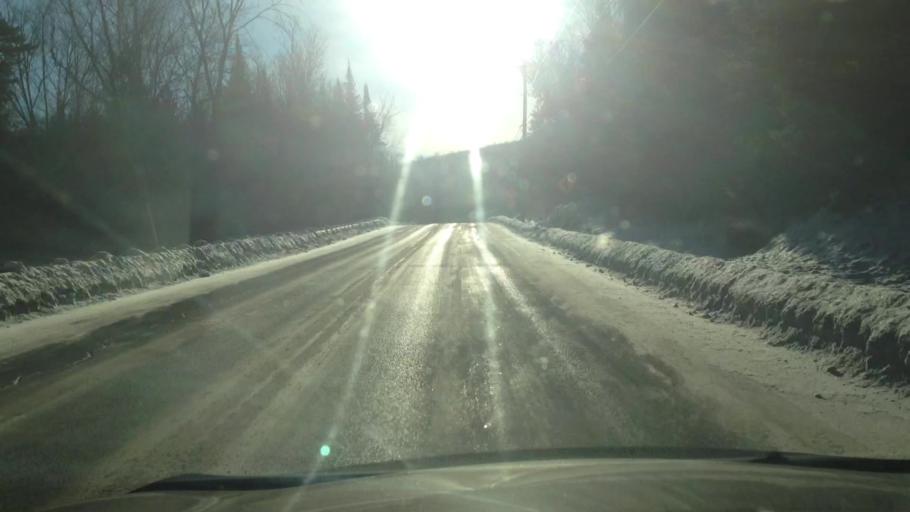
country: CA
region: Quebec
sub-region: Laurentides
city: Sainte-Agathe-des-Monts
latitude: 45.9124
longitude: -74.3572
